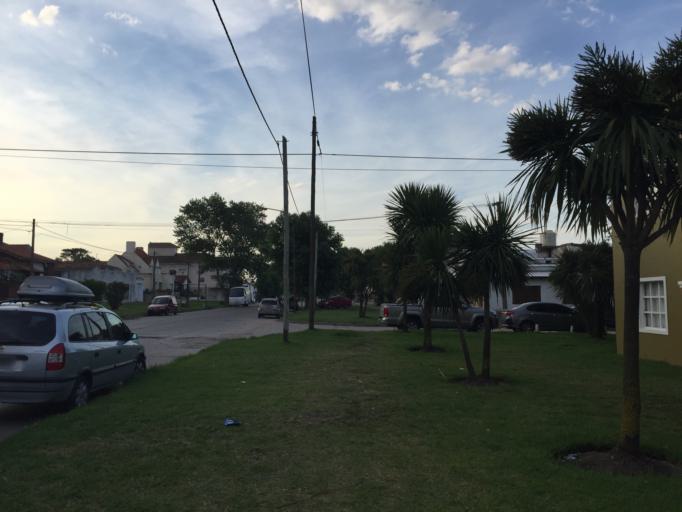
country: AR
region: Buenos Aires
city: Miramar
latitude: -38.2691
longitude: -57.8291
